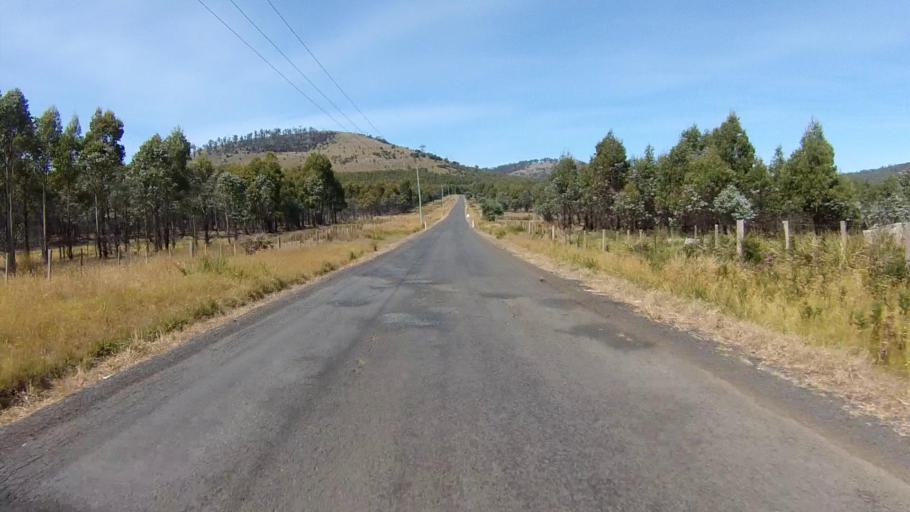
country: AU
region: Tasmania
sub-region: Sorell
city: Sorell
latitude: -42.6190
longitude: 147.7302
